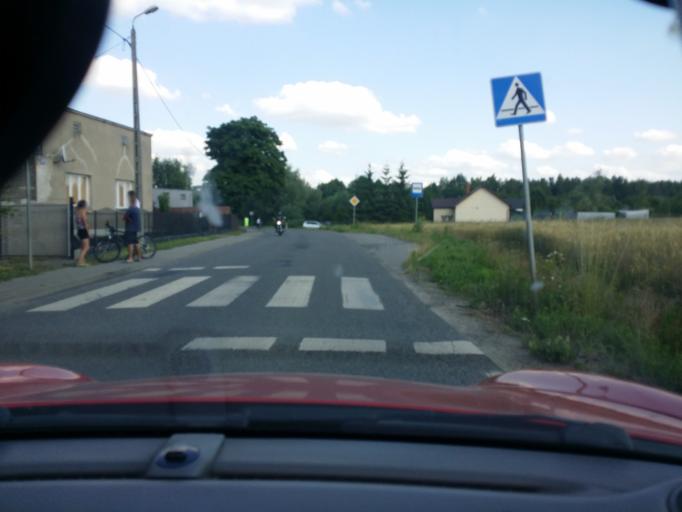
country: PL
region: Masovian Voivodeship
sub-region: Powiat radomski
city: Trablice
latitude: 51.3512
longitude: 21.1403
